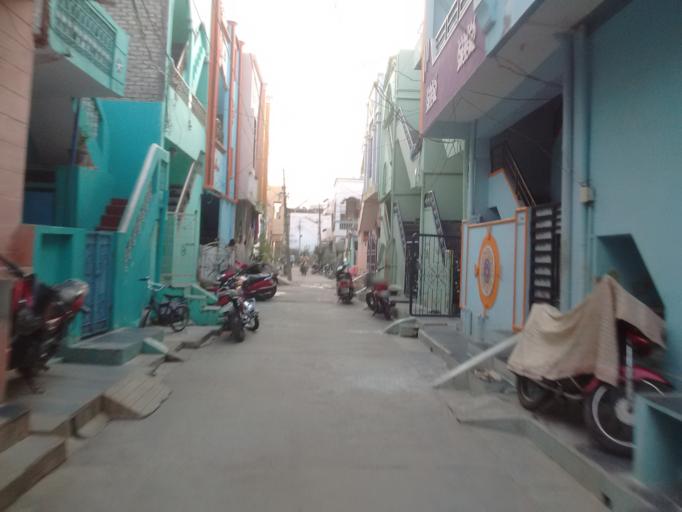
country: IN
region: Telangana
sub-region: Mahbubnagar
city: Alampur
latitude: 15.8117
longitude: 78.0447
